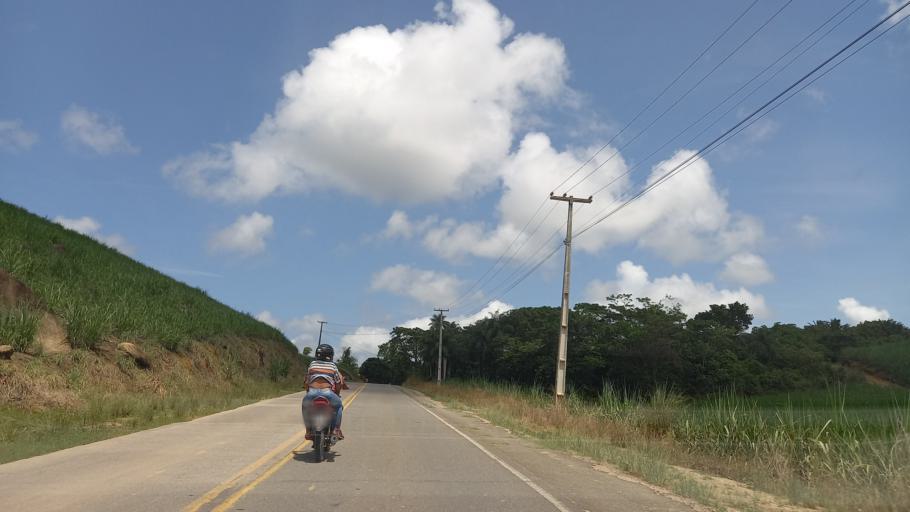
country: BR
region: Pernambuco
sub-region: Sirinhaem
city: Sirinhaem
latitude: -8.6117
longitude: -35.1194
